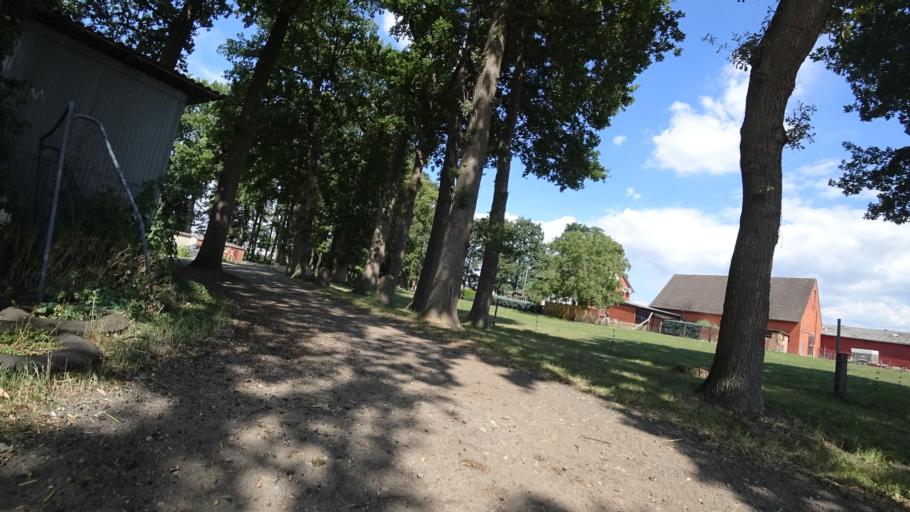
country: DE
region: North Rhine-Westphalia
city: Rietberg
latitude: 51.8763
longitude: 8.4446
